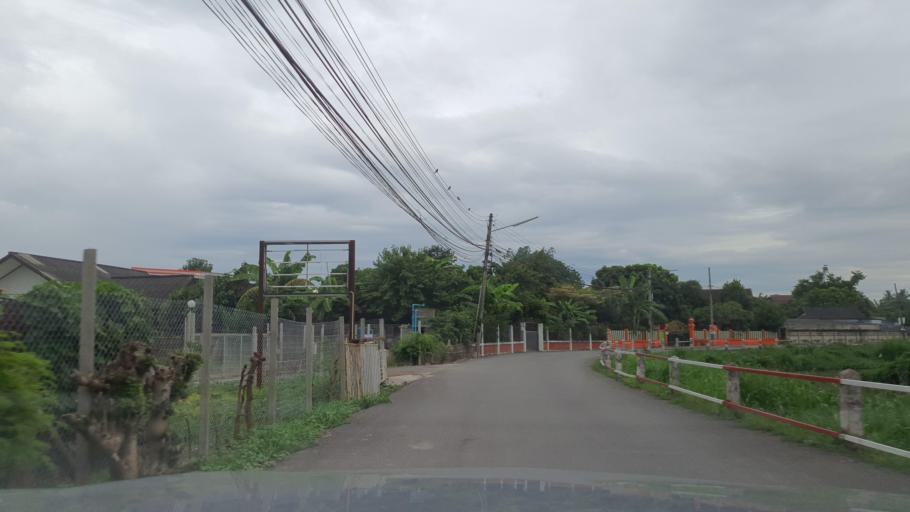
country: TH
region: Chiang Mai
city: San Sai
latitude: 18.9230
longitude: 98.9428
